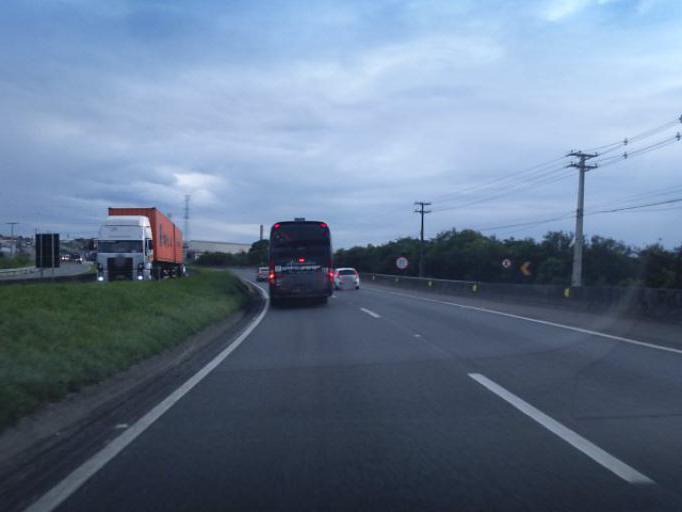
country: BR
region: Parana
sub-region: Sao Jose Dos Pinhais
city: Sao Jose dos Pinhais
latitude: -25.5967
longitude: -49.1739
